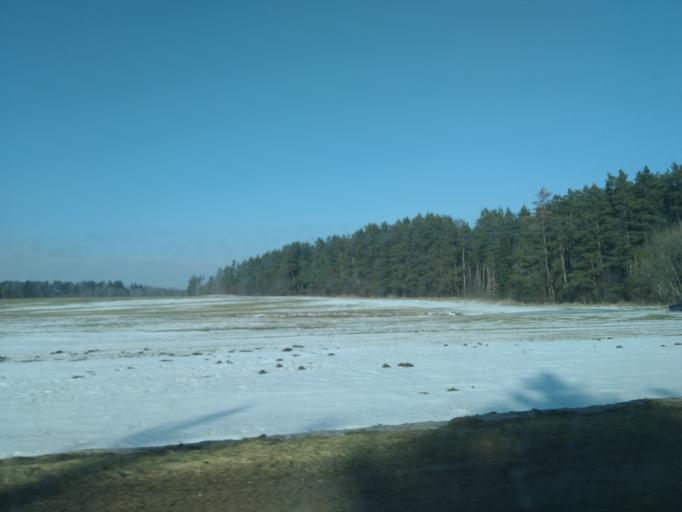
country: BY
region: Minsk
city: Snow
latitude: 53.2021
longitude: 26.5123
